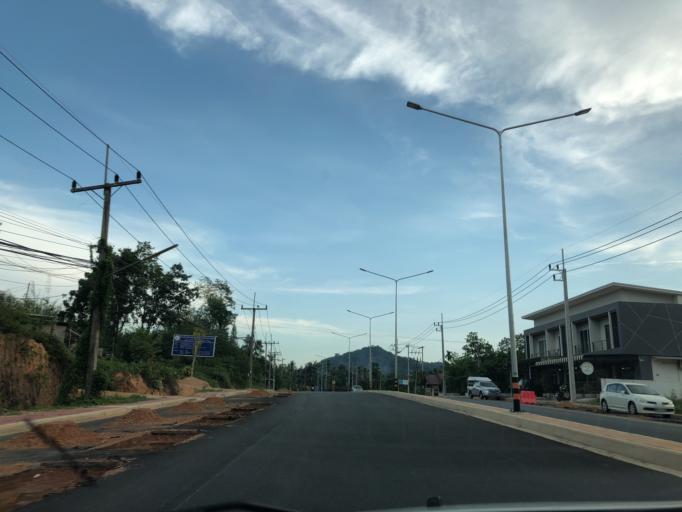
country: TH
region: Phangnga
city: Ban Ao Nang
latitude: 8.0637
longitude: 98.8427
